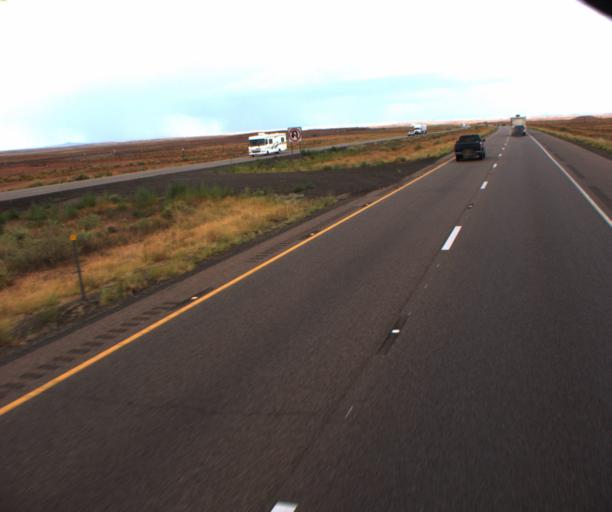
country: US
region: Arizona
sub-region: Coconino County
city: LeChee
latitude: 35.0883
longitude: -110.9030
